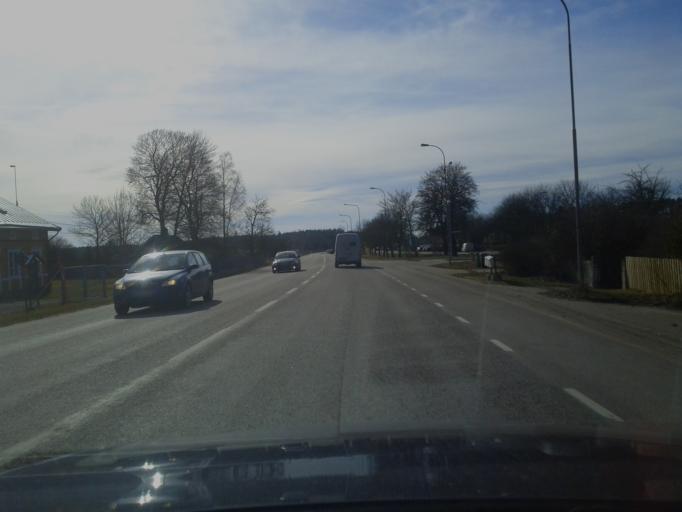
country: SE
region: Soedermanland
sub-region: Eskilstuna Kommun
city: Kvicksund
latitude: 59.5731
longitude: 16.3932
